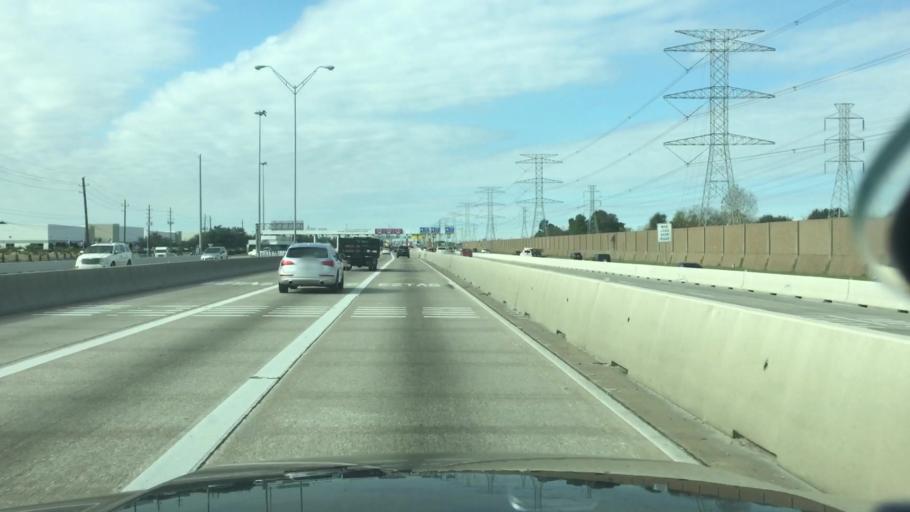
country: US
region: Texas
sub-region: Harris County
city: Hudson
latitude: 29.9378
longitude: -95.4683
